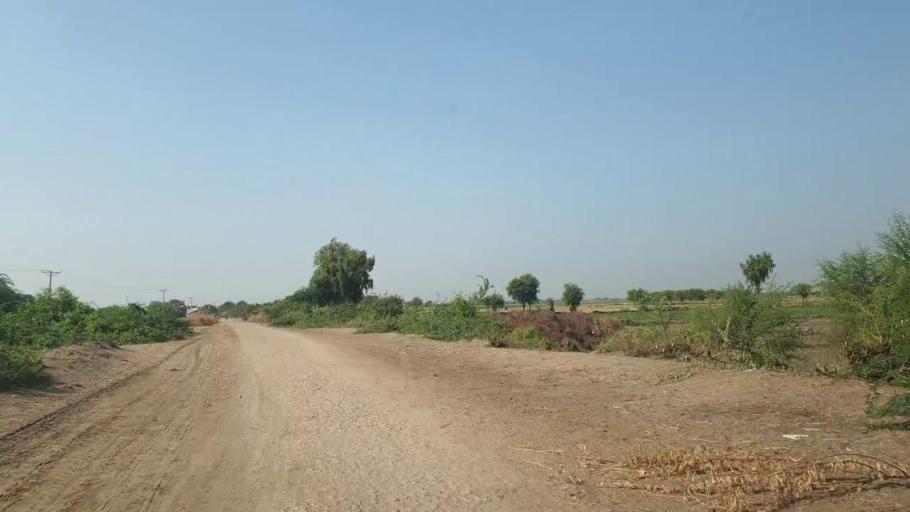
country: PK
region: Sindh
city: Badin
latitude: 24.5207
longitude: 68.7868
